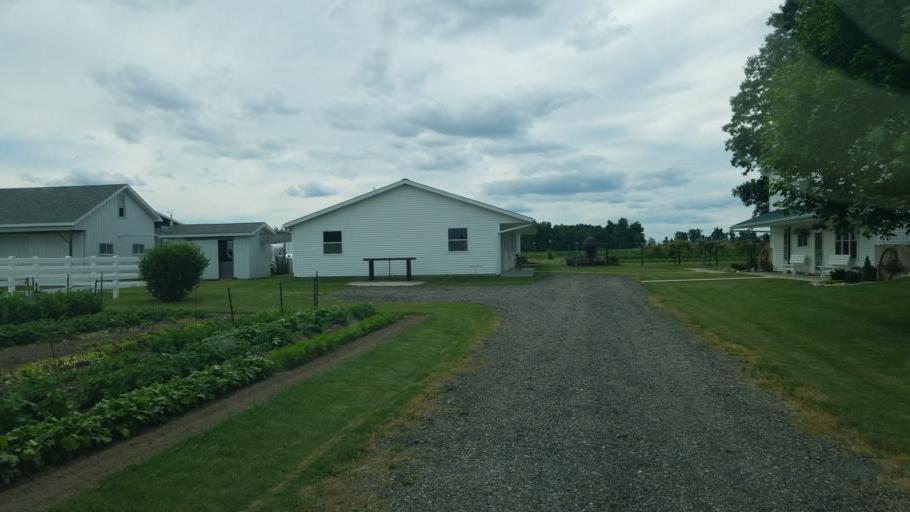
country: US
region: Michigan
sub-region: Barry County
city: Nashville
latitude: 42.6775
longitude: -84.9757
